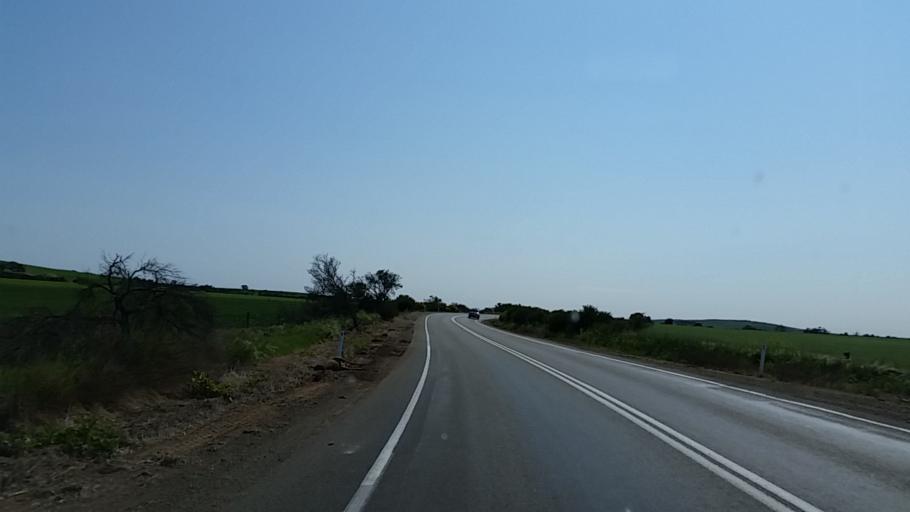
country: AU
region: South Australia
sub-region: Northern Areas
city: Jamestown
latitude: -33.2341
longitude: 138.3914
